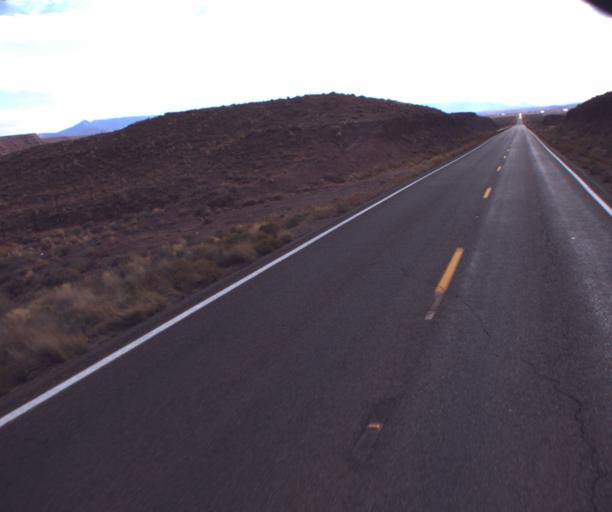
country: US
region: Arizona
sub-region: Apache County
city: Many Farms
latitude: 36.5401
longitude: -109.5221
